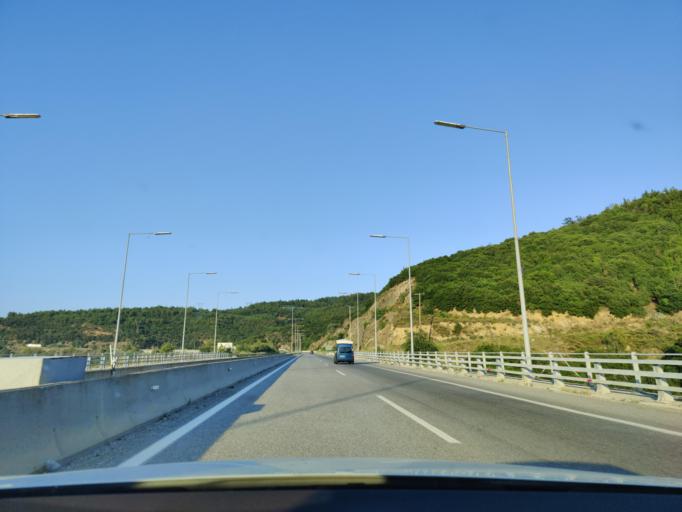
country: GR
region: East Macedonia and Thrace
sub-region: Nomos Kavalas
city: Kavala
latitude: 40.9549
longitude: 24.3855
